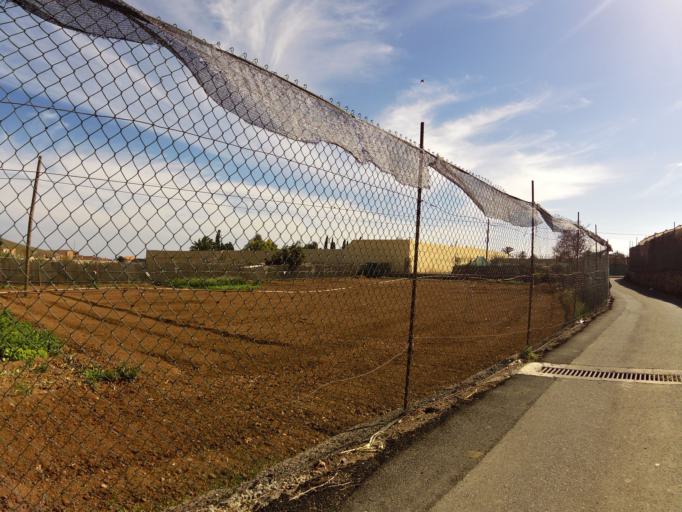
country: ES
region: Canary Islands
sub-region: Provincia de Las Palmas
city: Aguimes
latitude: 27.9059
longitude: -15.4499
